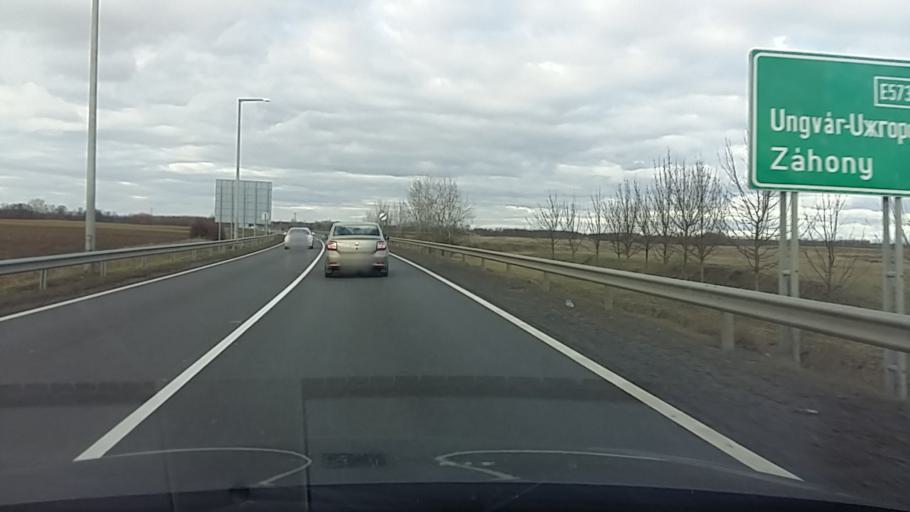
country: HU
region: Szabolcs-Szatmar-Bereg
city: Nyirpazony
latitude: 47.9530
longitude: 21.8206
